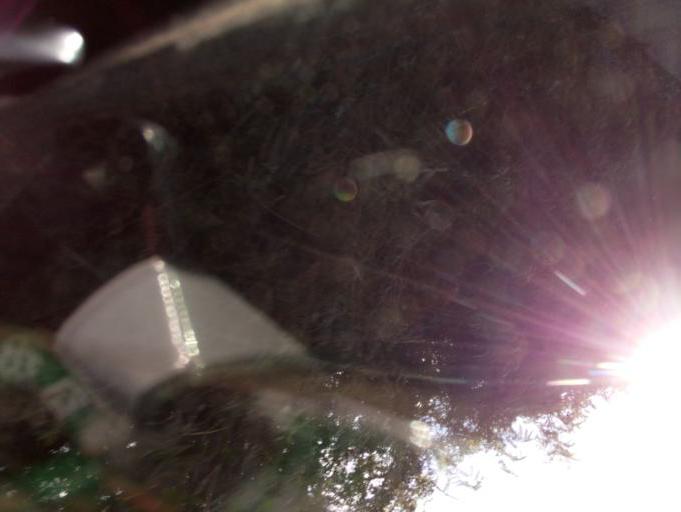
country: GB
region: England
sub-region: Devon
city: Dartmouth
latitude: 50.3467
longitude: -3.6483
